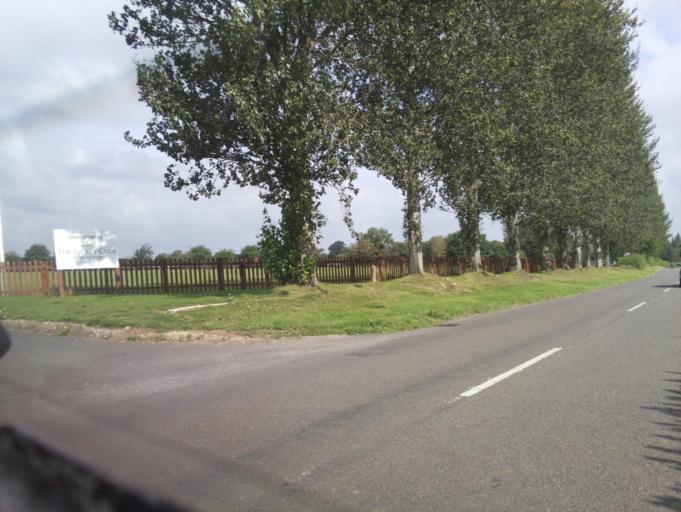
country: GB
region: England
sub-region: Somerset
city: Wincanton
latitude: 51.0671
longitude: -2.4126
